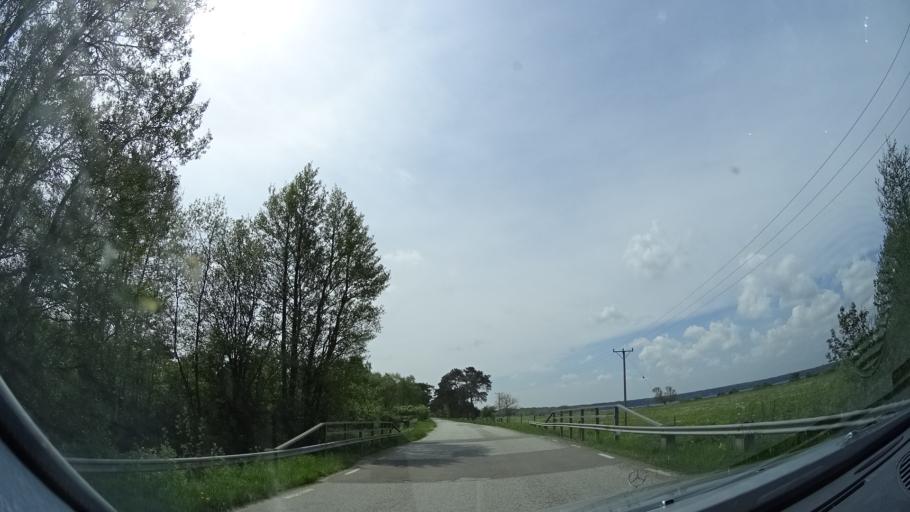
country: SE
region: Skane
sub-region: Sjobo Kommun
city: Sjoebo
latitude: 55.6784
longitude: 13.6281
